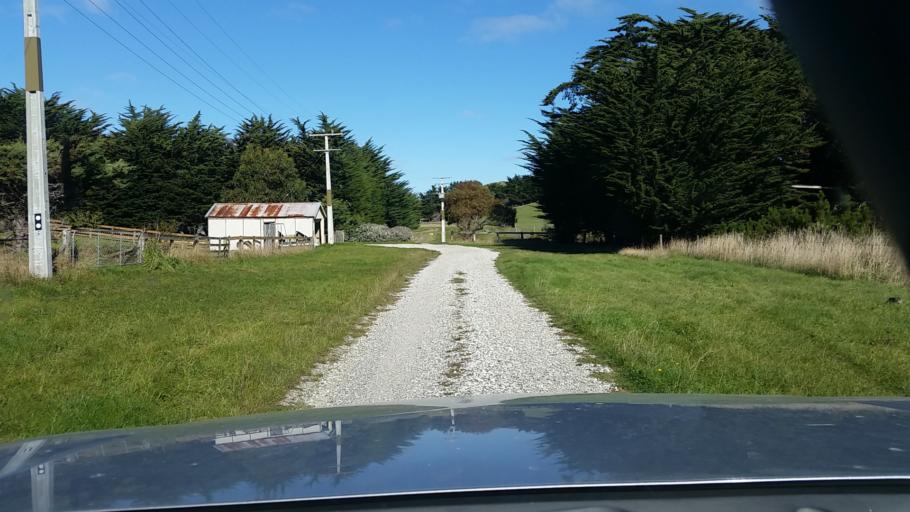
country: NZ
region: Marlborough
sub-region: Marlborough District
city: Blenheim
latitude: -41.7409
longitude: 174.1668
